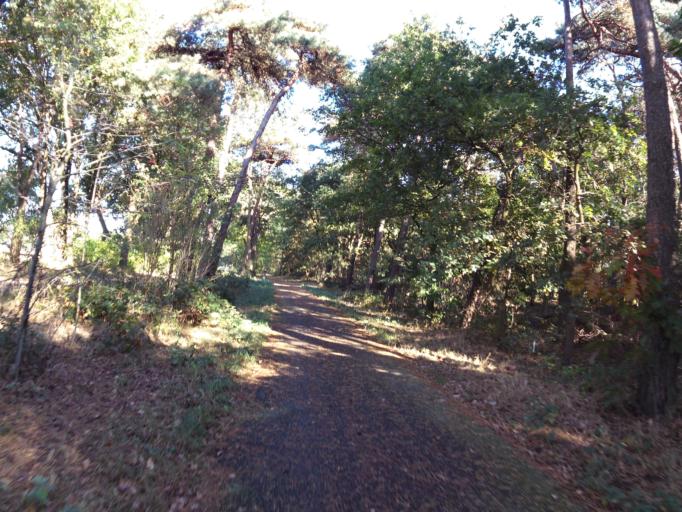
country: NL
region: Limburg
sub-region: Gemeente Venlo
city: Arcen
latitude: 51.4259
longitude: 6.2078
